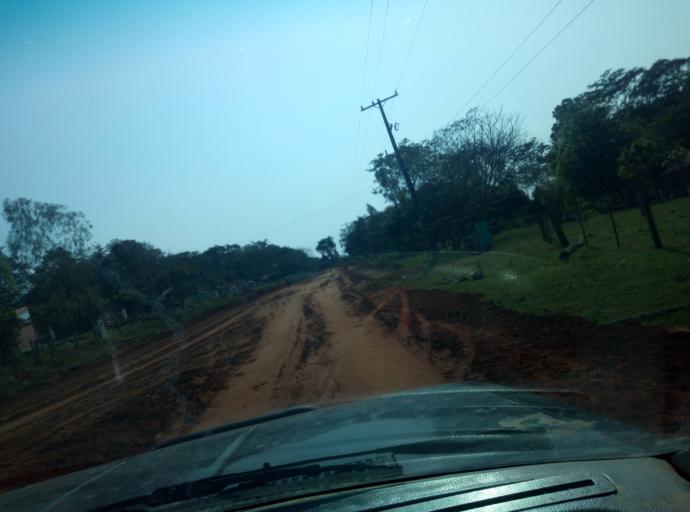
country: PY
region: Caaguazu
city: Carayao
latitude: -25.3085
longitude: -56.3254
